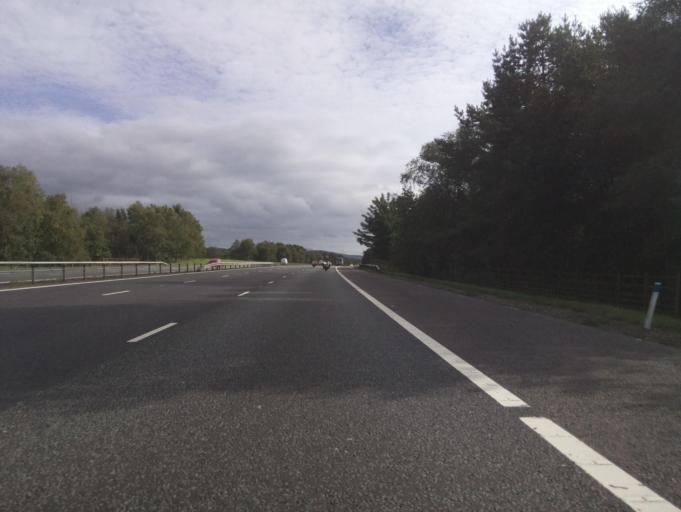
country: GB
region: Scotland
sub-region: Dumfries and Galloway
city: Lochmaben
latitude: 55.1736
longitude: -3.3973
